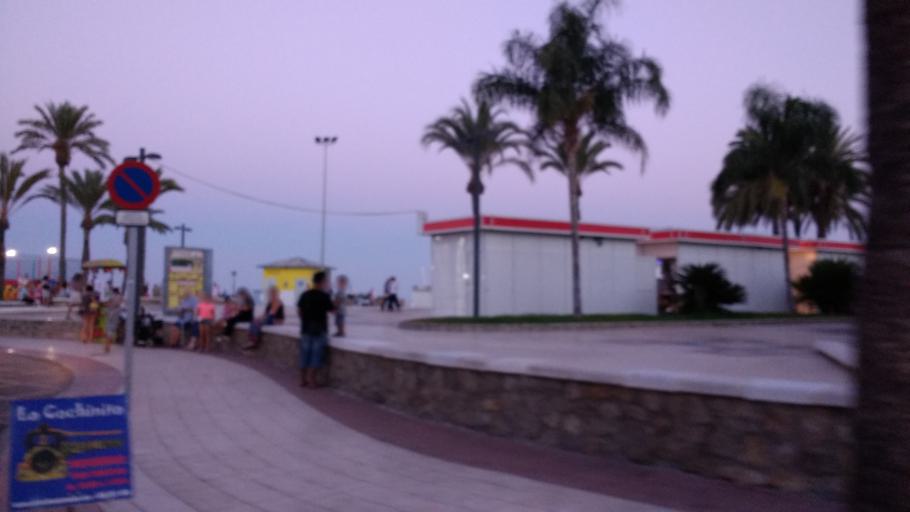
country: ES
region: Andalusia
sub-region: Provincia de Malaga
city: Velez-Malaga
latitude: 36.7399
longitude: -4.0919
